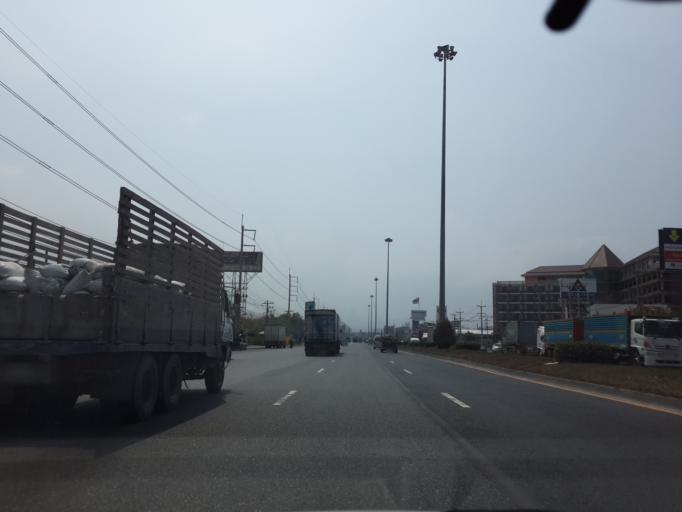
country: TH
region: Chon Buri
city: Chon Buri
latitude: 13.4160
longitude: 100.9985
